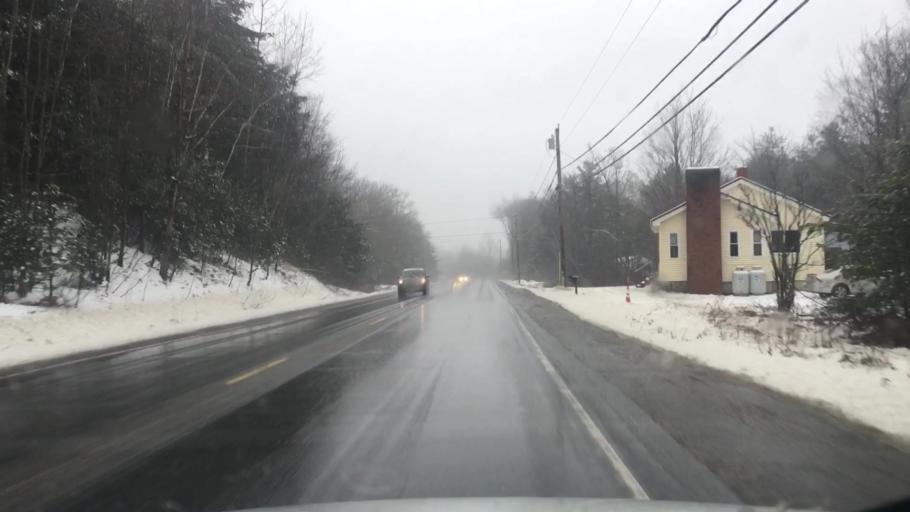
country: US
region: Maine
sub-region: Cumberland County
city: Gorham
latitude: 43.6828
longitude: -70.4735
